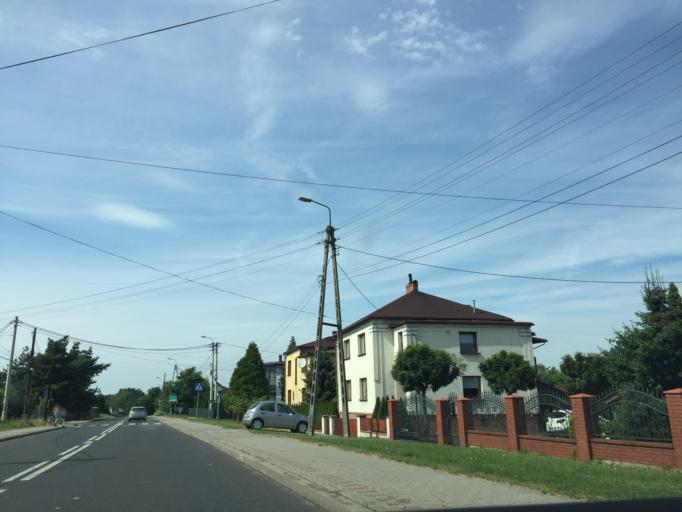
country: PL
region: Silesian Voivodeship
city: Gorzyczki
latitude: 49.9540
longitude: 18.4015
